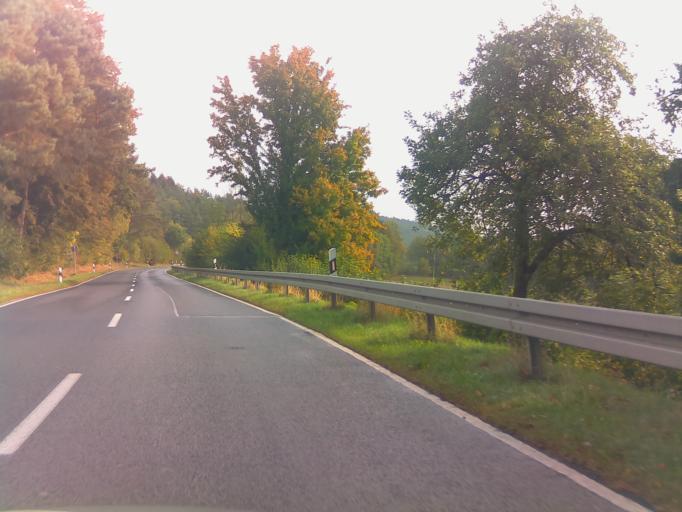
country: DE
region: Hesse
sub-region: Regierungsbezirk Kassel
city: Neuhof
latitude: 50.5088
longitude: 9.5724
